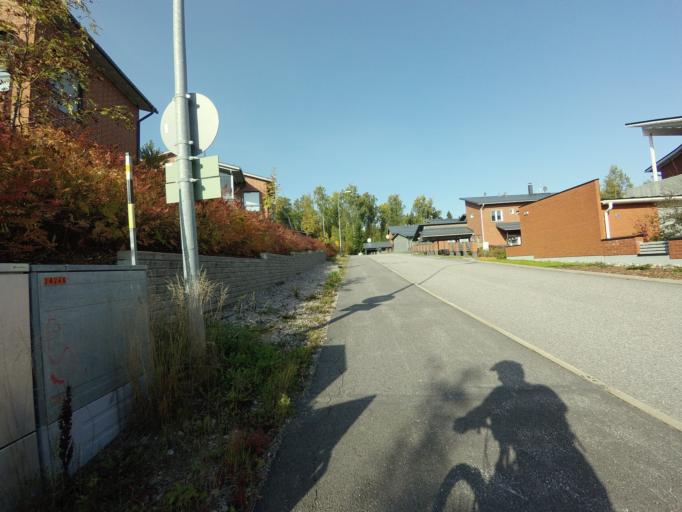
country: FI
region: Uusimaa
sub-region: Helsinki
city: Espoo
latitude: 60.1726
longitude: 24.6439
